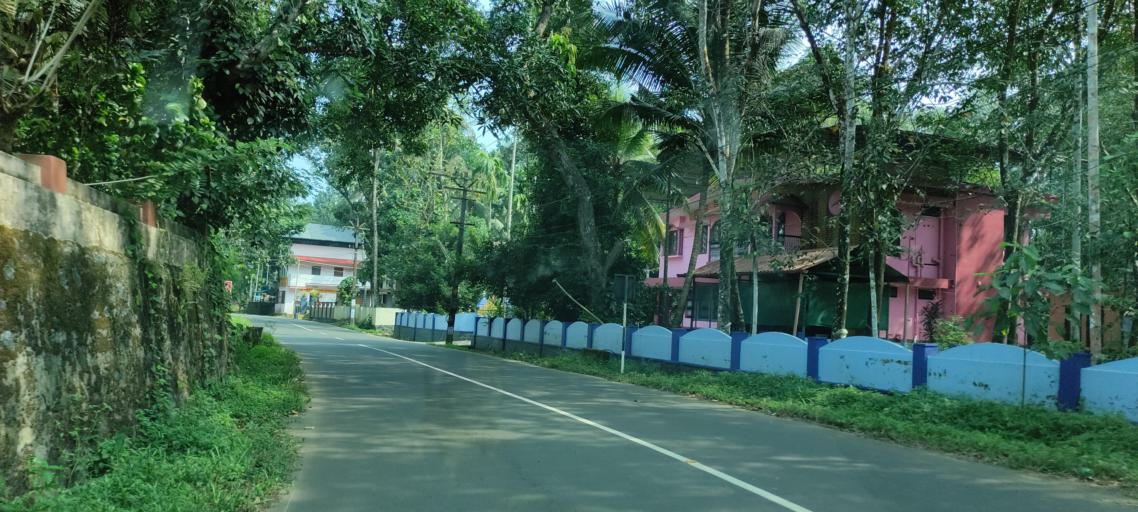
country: IN
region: Kerala
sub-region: Pattanamtitta
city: Adur
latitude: 9.2279
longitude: 76.7039
